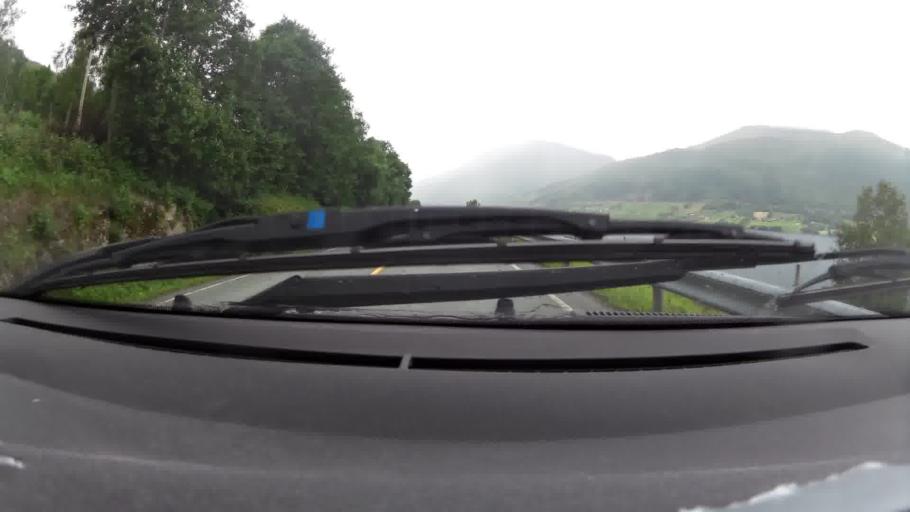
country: NO
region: More og Romsdal
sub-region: Gjemnes
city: Batnfjordsora
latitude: 62.9139
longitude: 7.7312
